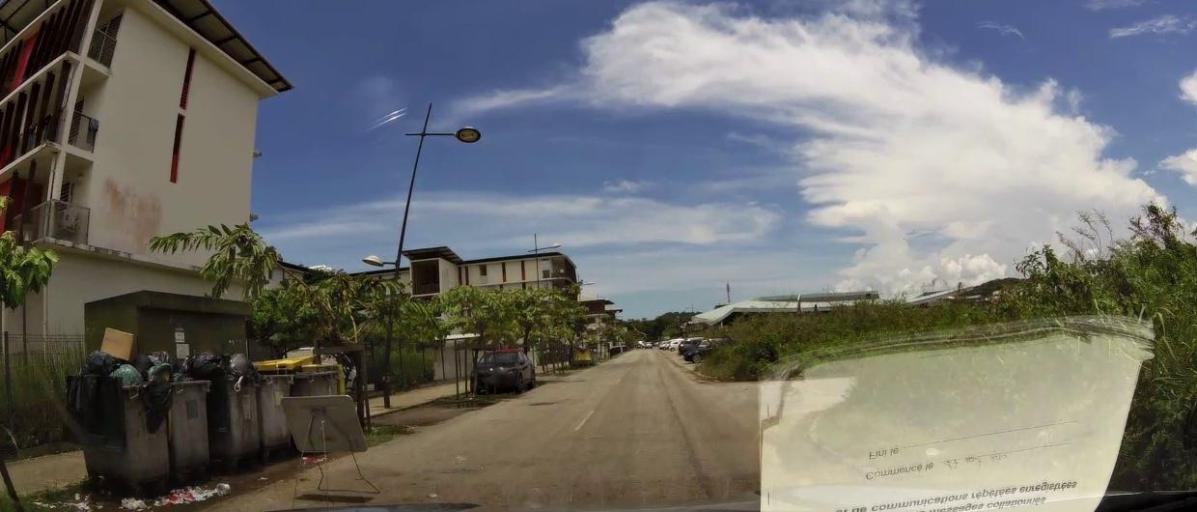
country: GF
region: Guyane
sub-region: Guyane
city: Cayenne
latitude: 4.9345
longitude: -52.3029
